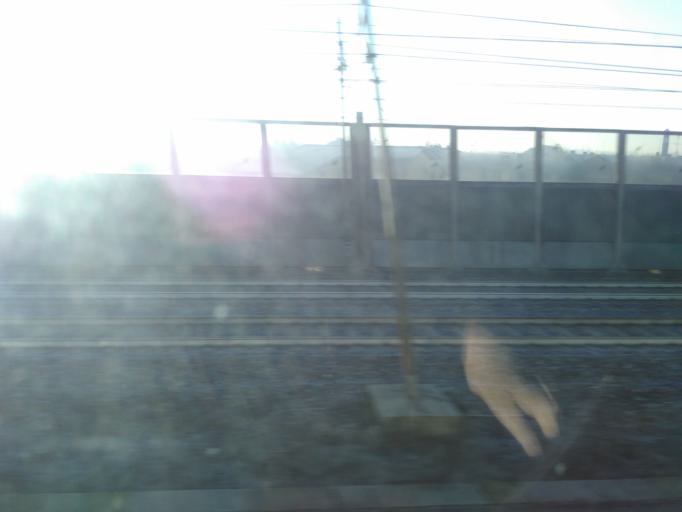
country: IT
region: Veneto
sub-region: Provincia di Padova
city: Vigonza
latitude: 45.4337
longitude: 11.9702
